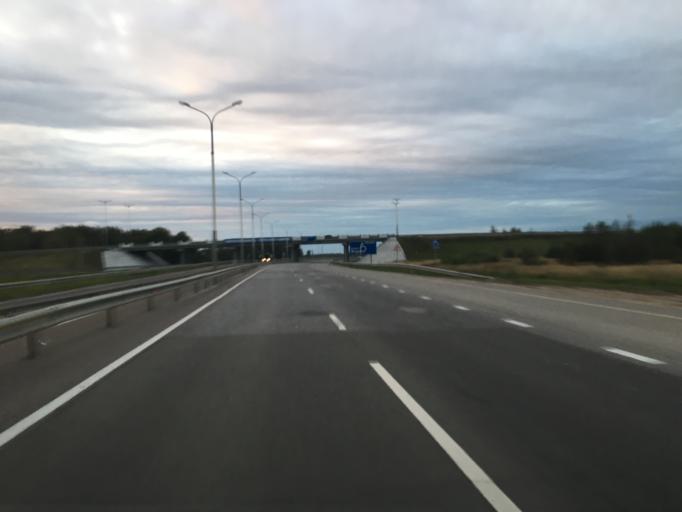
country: RU
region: Kaluga
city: Kaluga
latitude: 54.6233
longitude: 36.2908
